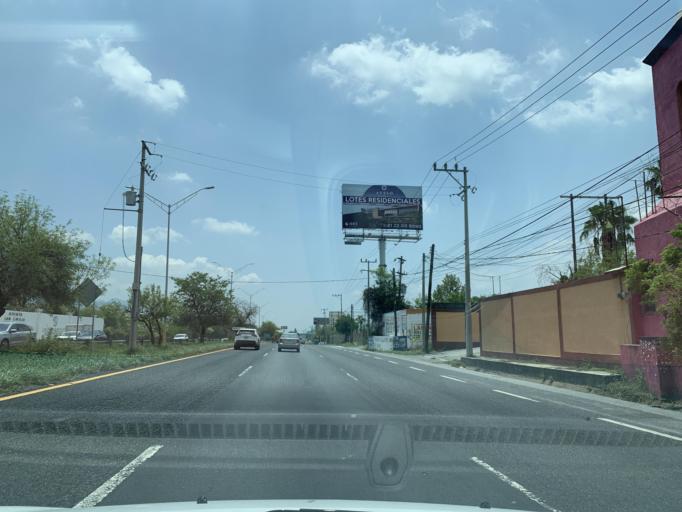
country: MX
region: Nuevo Leon
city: Santiago
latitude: 25.4910
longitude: -100.1855
